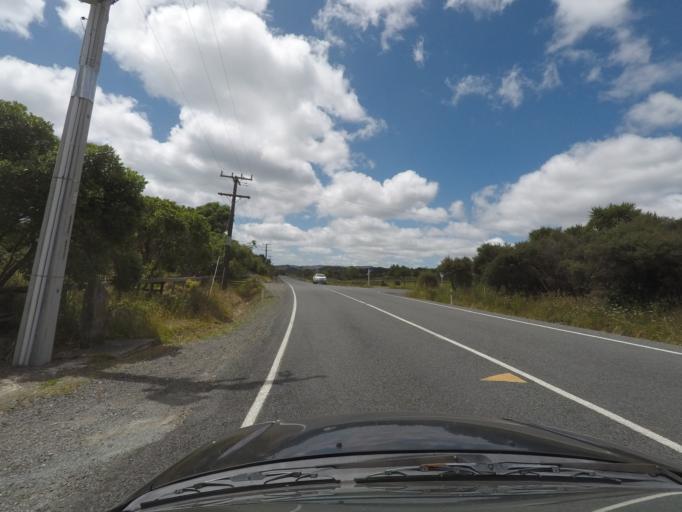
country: NZ
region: Northland
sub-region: Whangarei
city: Ruakaka
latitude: -36.0204
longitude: 174.4937
